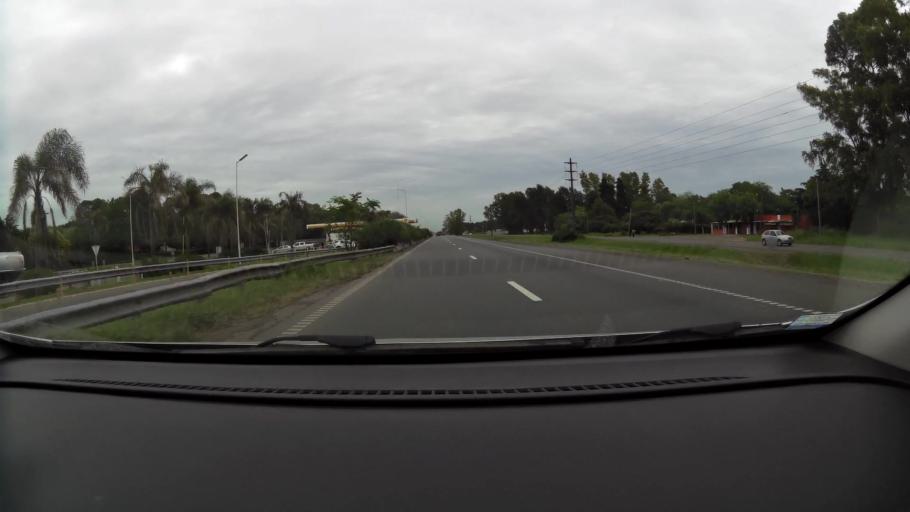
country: AR
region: Buenos Aires
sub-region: Partido de Zarate
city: Zarate
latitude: -34.1109
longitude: -59.1225
